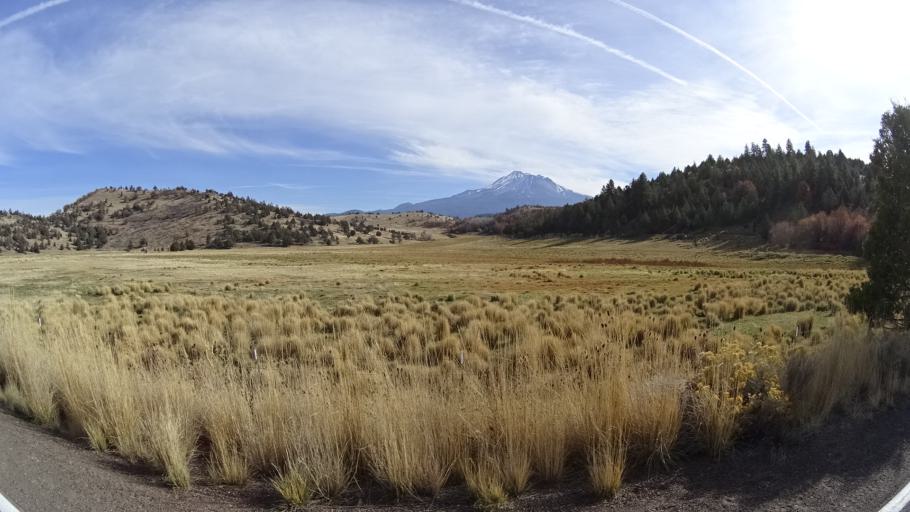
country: US
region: California
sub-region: Siskiyou County
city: Weed
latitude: 41.4818
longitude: -122.4103
